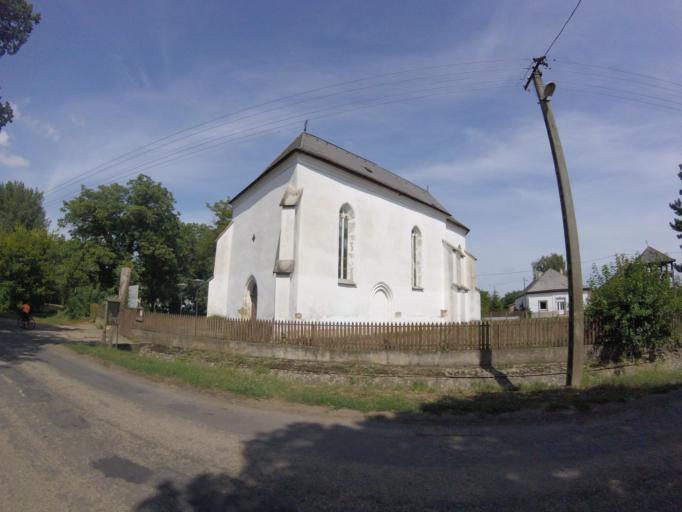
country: HU
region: Szabolcs-Szatmar-Bereg
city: Csenger
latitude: 47.9336
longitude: 22.6594
